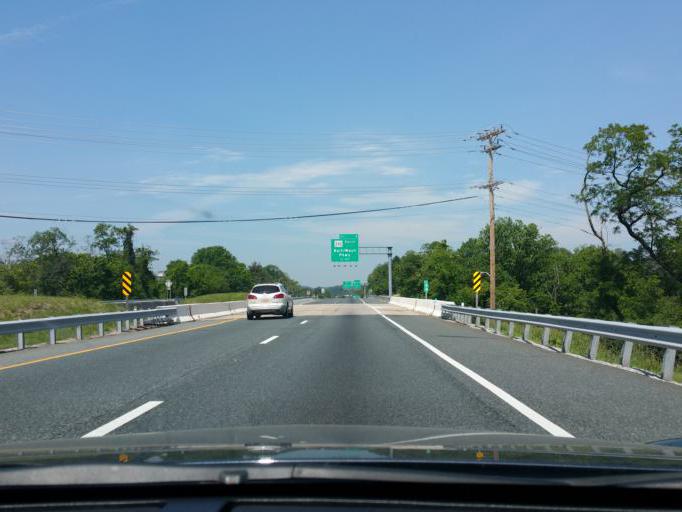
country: US
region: Maryland
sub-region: Baltimore County
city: Baltimore Highlands
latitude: 39.2307
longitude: -76.6410
